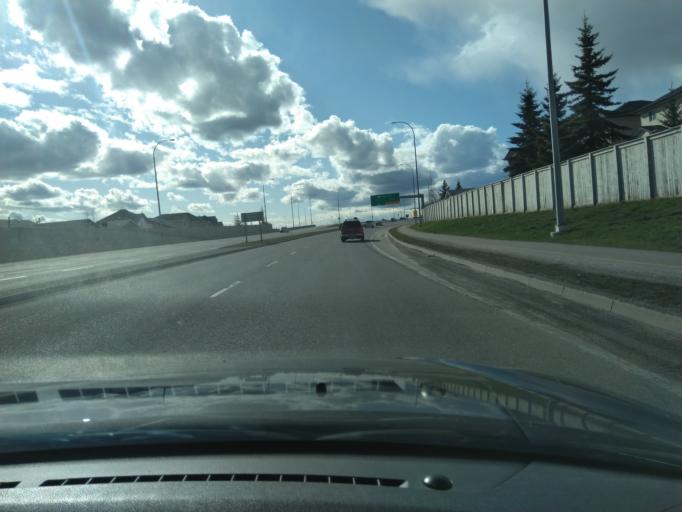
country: CA
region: Alberta
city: Calgary
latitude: 51.1428
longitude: -114.1965
